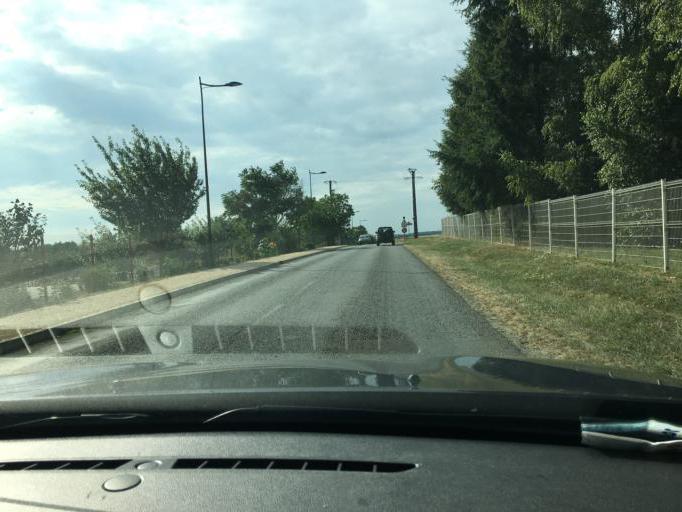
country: FR
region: Centre
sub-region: Departement du Cher
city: Rians
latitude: 47.1906
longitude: 2.6056
